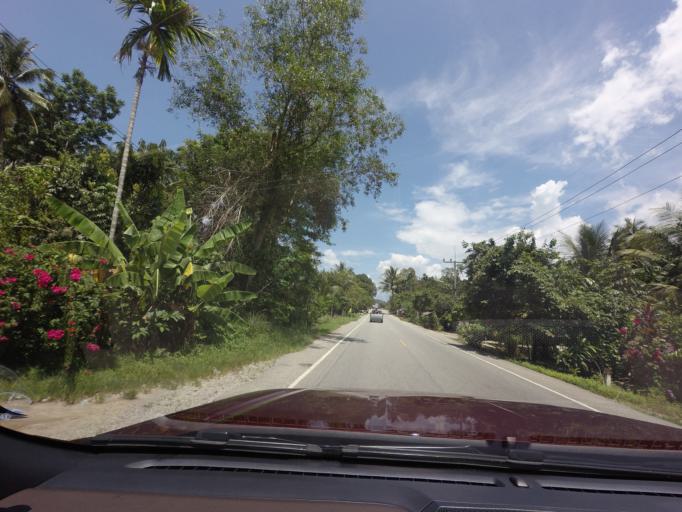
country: TH
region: Narathiwat
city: Chanae
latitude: 6.1345
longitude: 101.6990
